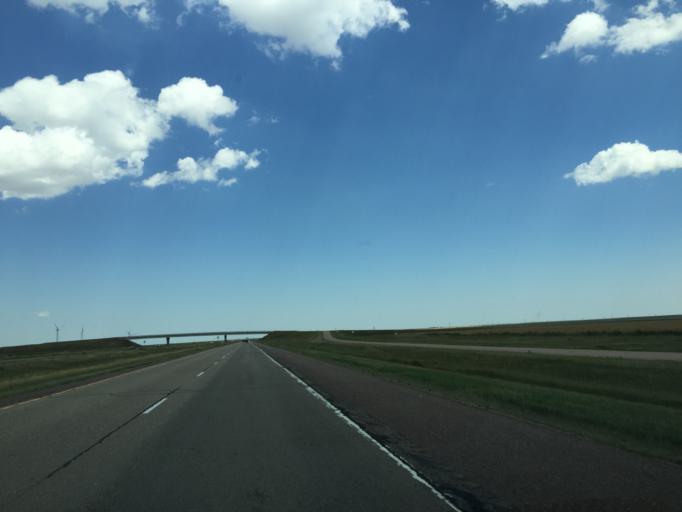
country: US
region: Colorado
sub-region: Lincoln County
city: Hugo
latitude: 39.2777
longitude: -103.4414
